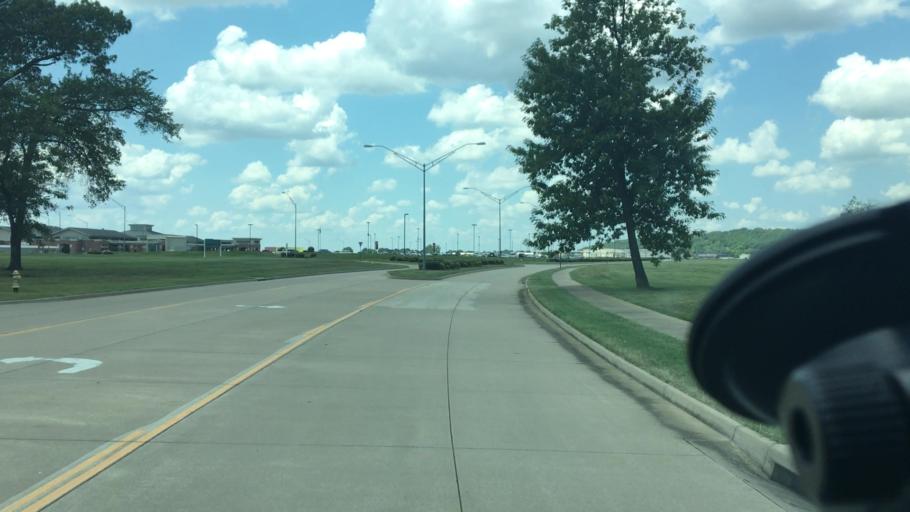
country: US
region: Arkansas
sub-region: Sebastian County
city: Barling
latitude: 35.3429
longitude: -94.3553
